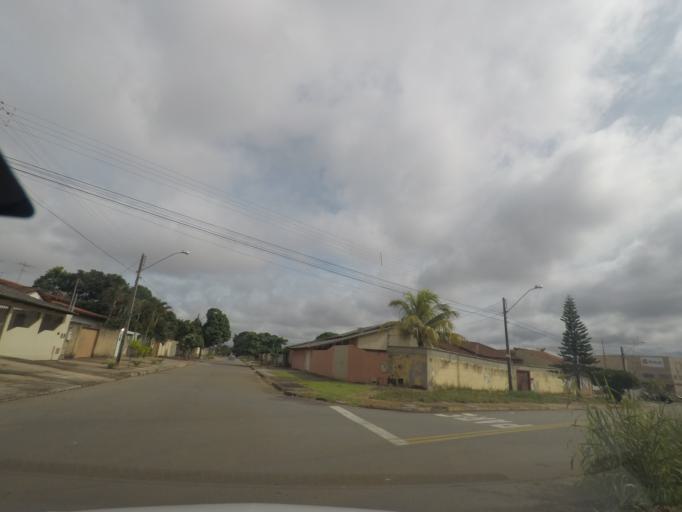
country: BR
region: Goias
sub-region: Goiania
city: Goiania
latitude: -16.7421
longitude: -49.3257
